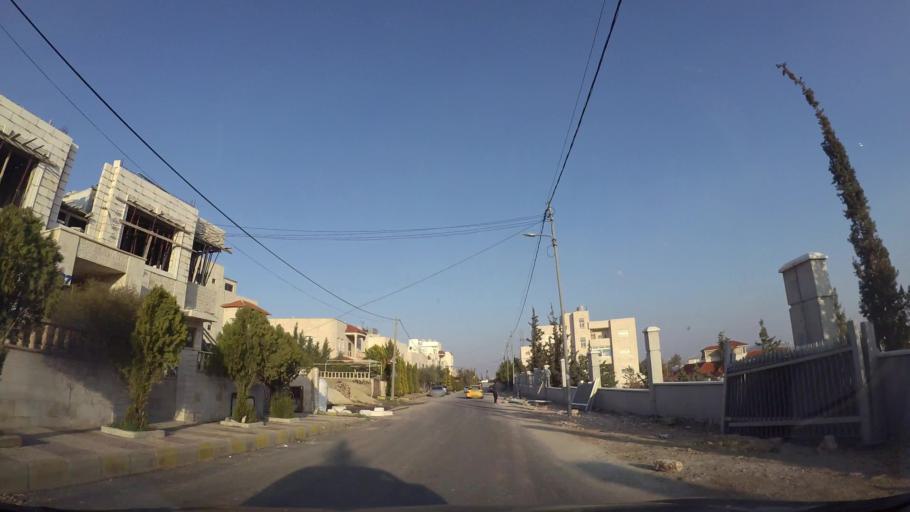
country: JO
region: Amman
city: Amman
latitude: 31.9844
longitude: 35.9654
